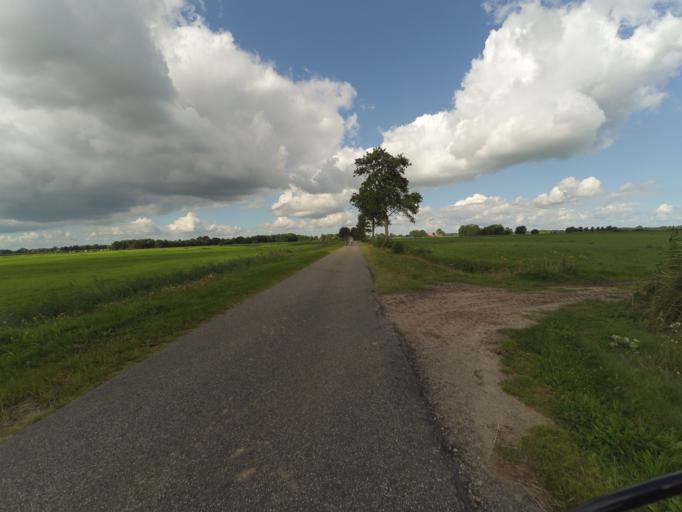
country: NL
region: Friesland
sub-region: Gemeente Tytsjerksteradiel
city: Hurdegaryp
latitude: 53.2348
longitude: 5.9332
